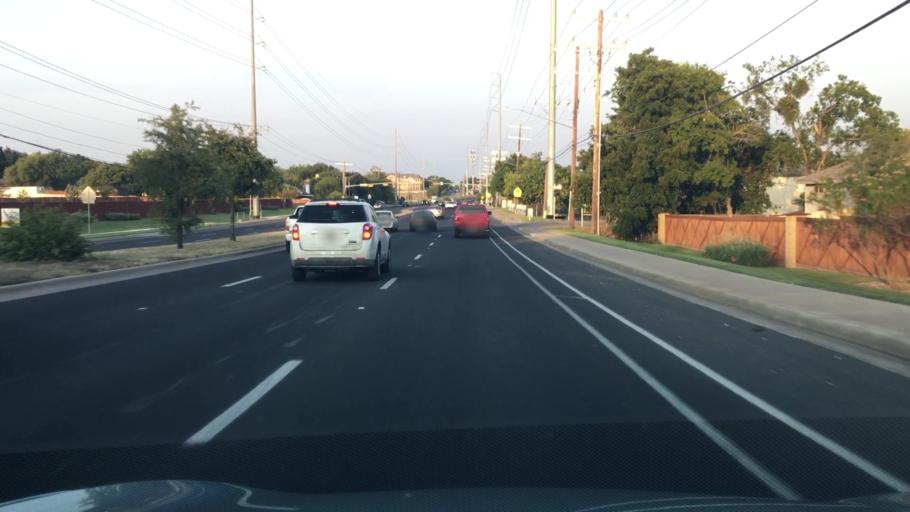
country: US
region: Texas
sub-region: Travis County
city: Manchaca
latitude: 30.1739
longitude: -97.8082
